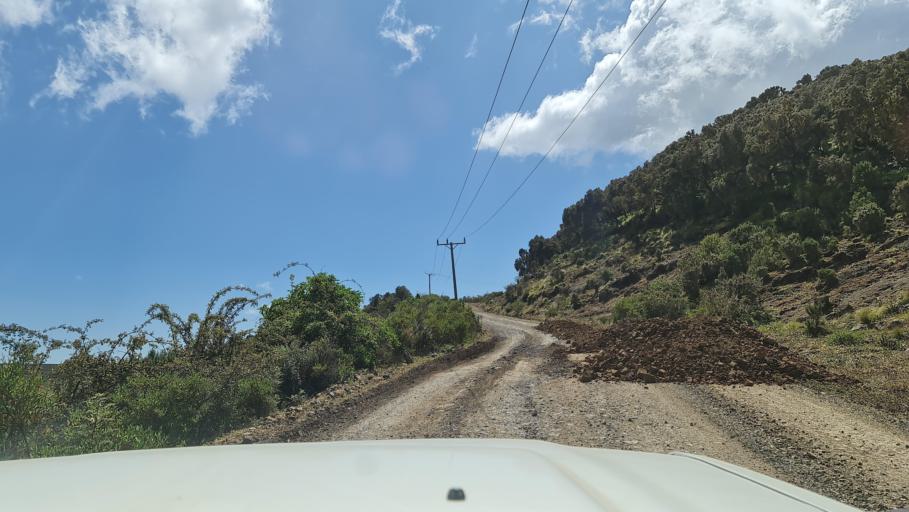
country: ET
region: Amhara
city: Debark'
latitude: 13.2235
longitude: 38.0149
